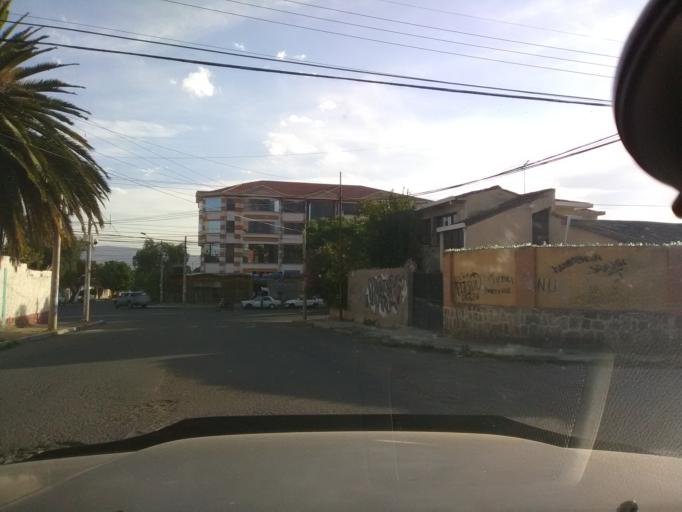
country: BO
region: Cochabamba
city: Cochabamba
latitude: -17.3646
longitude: -66.1766
